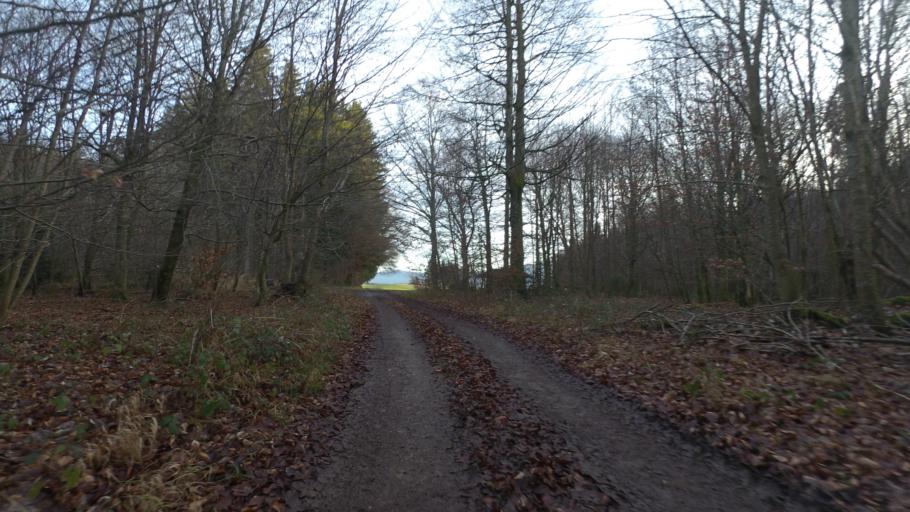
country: DE
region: Bavaria
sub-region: Upper Bavaria
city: Chieming
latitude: 47.8789
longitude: 12.5441
